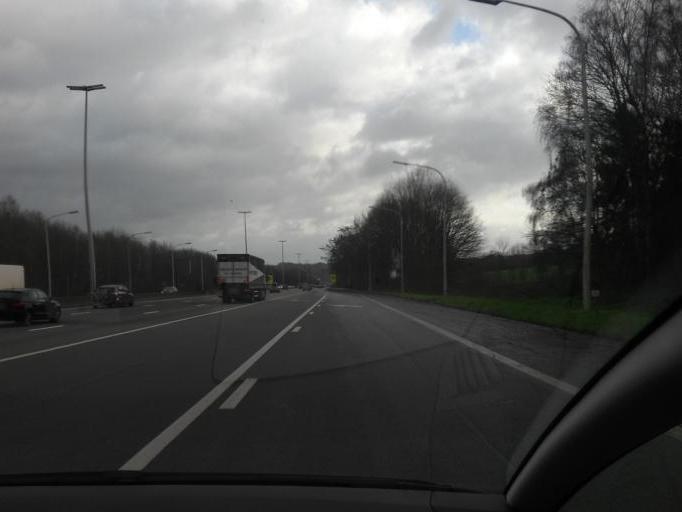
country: BE
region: Wallonia
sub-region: Province du Brabant Wallon
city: Wavre
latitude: 50.7168
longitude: 4.5876
